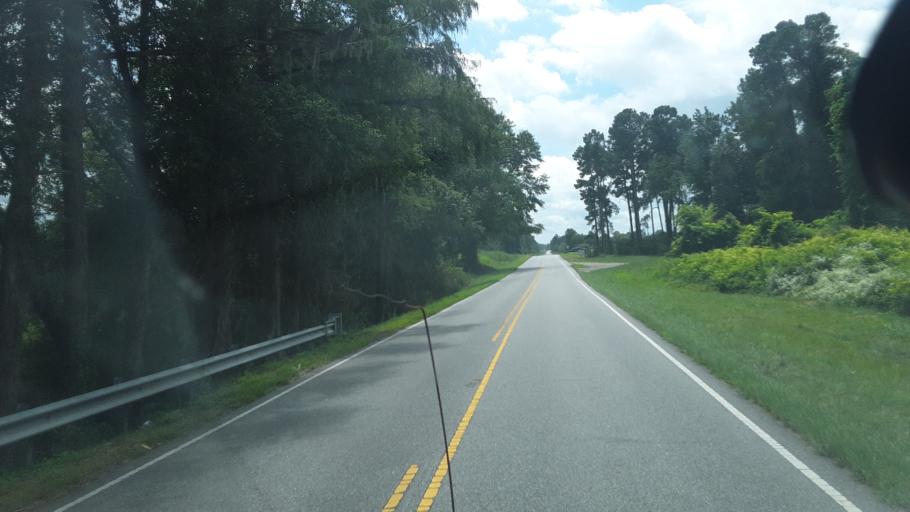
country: US
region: North Carolina
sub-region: Columbus County
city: Tabor City
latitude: 34.2751
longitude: -79.0415
